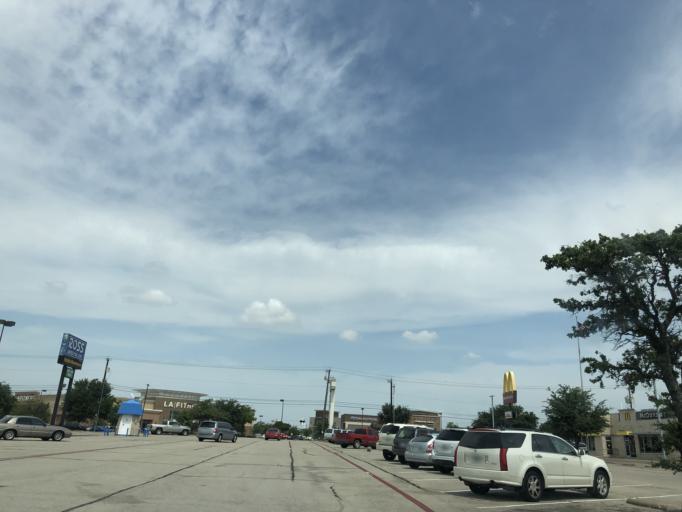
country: US
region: Texas
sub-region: Dallas County
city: Garland
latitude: 32.8571
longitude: -96.6456
